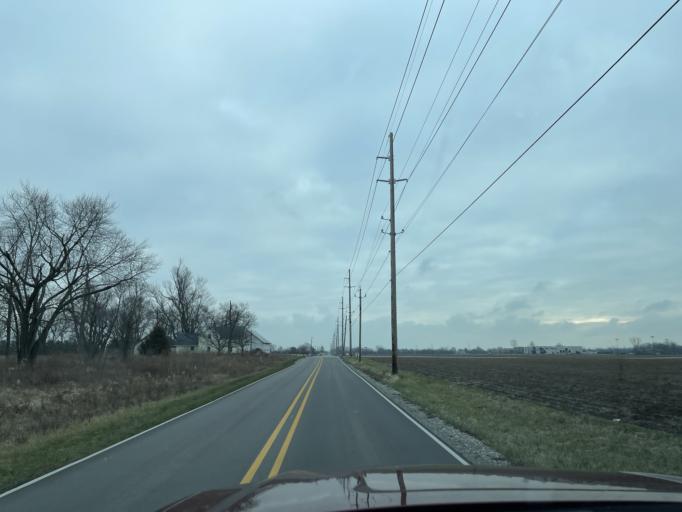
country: US
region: Indiana
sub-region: Boone County
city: Whitestown
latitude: 39.9457
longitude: -86.3719
